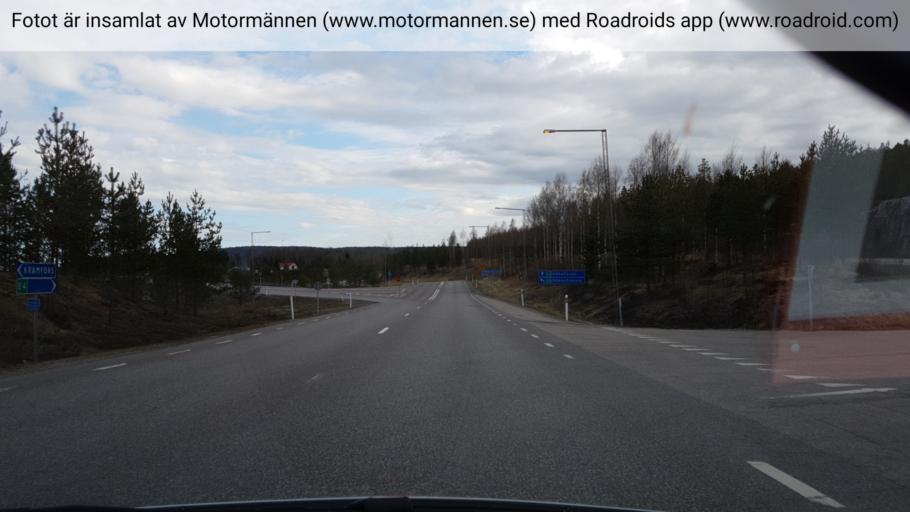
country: SE
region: Vaesternorrland
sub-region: Haernoesands Kommun
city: Haernoesand
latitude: 62.7871
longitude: 17.9176
